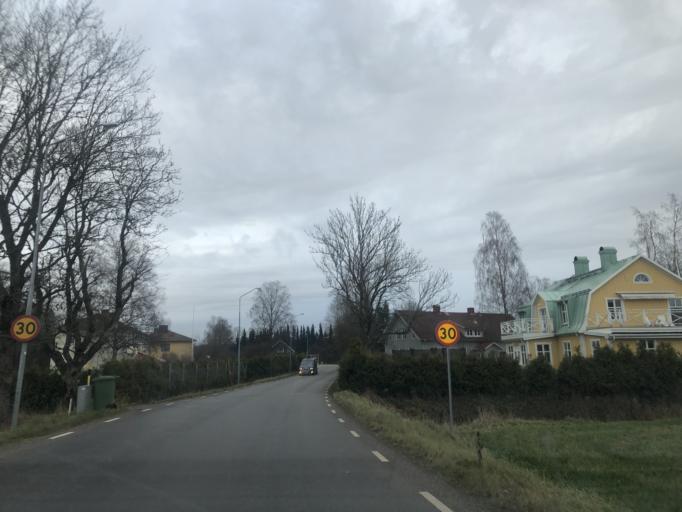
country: SE
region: Vaestra Goetaland
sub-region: Ulricehamns Kommun
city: Ulricehamn
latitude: 57.7983
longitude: 13.3729
